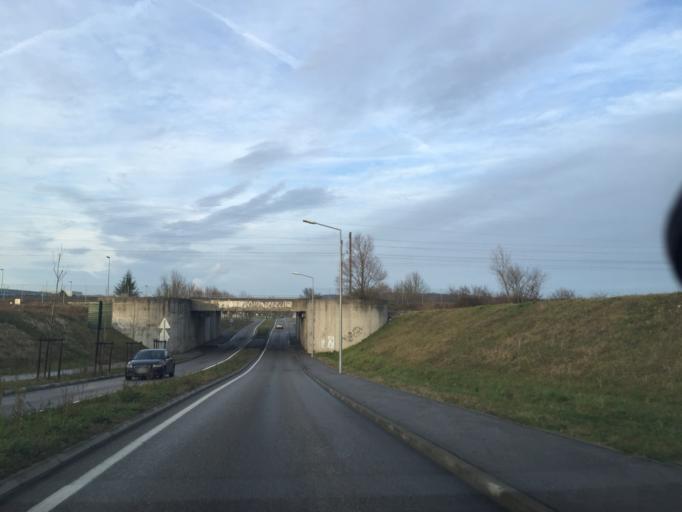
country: FR
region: Rhone-Alpes
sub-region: Departement de l'Isere
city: Vaulx-Milieu
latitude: 45.6182
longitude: 5.1736
